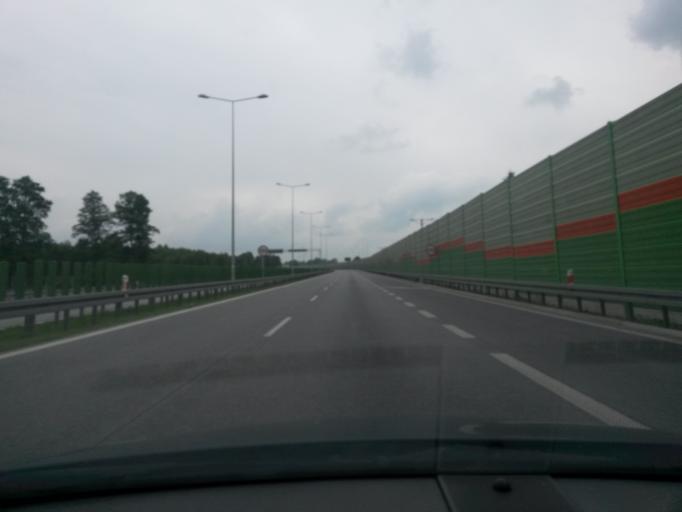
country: PL
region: Lodz Voivodeship
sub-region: Powiat rawski
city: Rawa Mazowiecka
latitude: 51.7481
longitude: 20.2428
